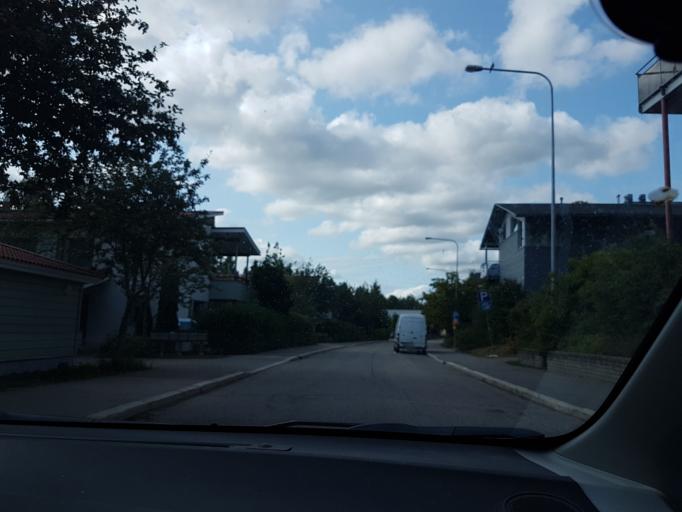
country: FI
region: Uusimaa
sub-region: Helsinki
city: Vantaa
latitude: 60.2269
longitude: 25.0538
